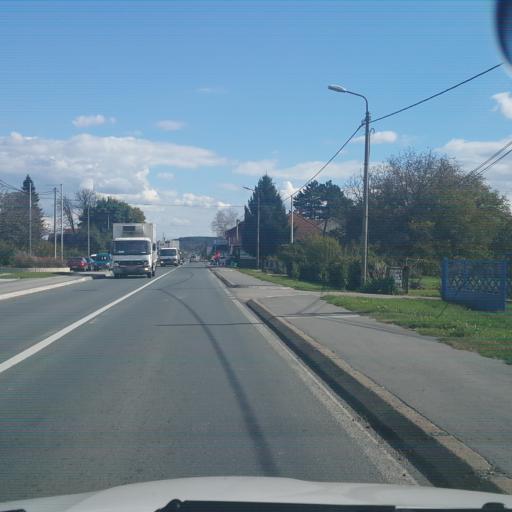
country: RS
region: Central Serbia
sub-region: Raski Okrug
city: Vrnjacka Banja
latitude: 43.6393
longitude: 20.9233
